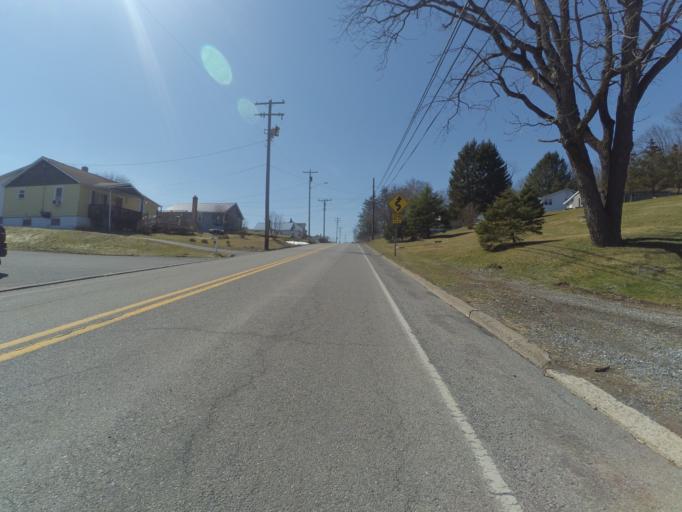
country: US
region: Pennsylvania
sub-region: Centre County
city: Bellefonte
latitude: 40.9104
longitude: -77.7958
